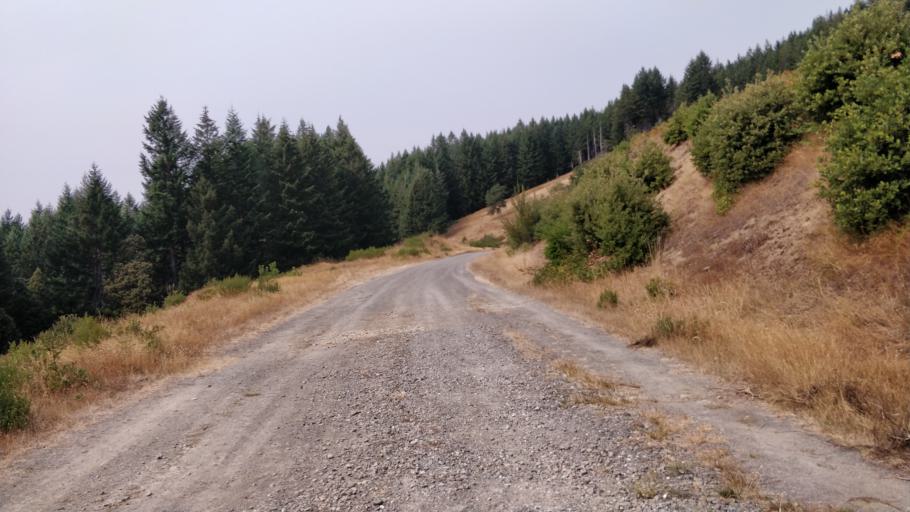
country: US
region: California
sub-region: Humboldt County
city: Westhaven-Moonstone
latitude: 41.2039
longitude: -123.9529
